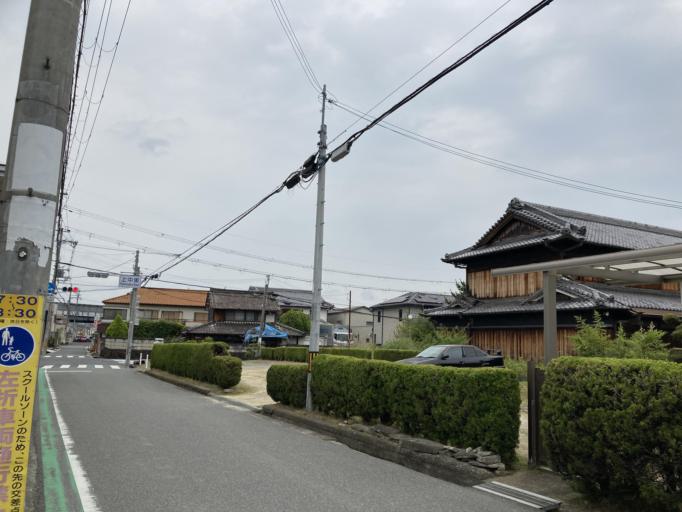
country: JP
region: Osaka
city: Kashihara
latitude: 34.5626
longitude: 135.7023
